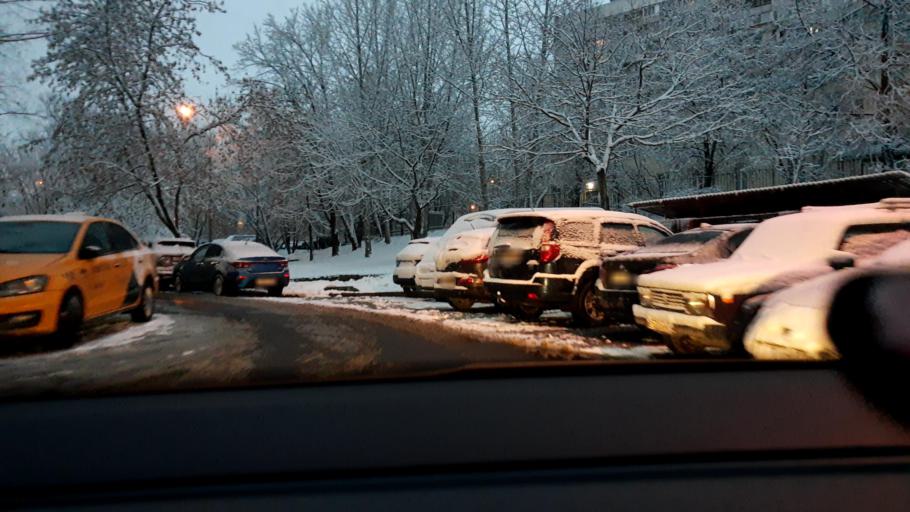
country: RU
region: Moscow
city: Lyublino
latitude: 55.6801
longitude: 37.7736
